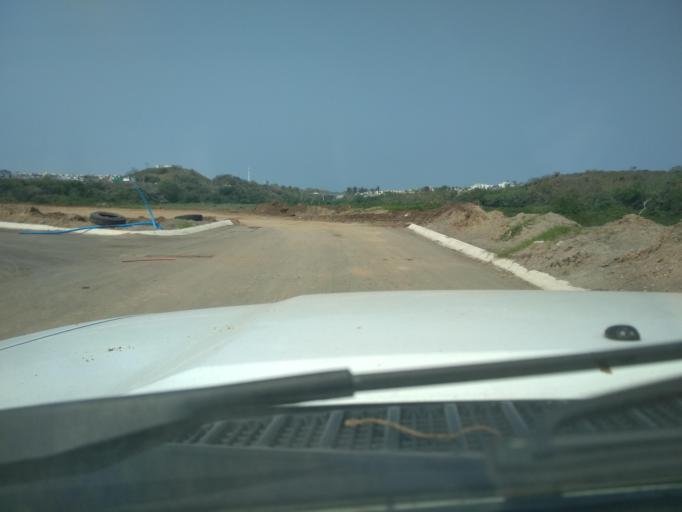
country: MX
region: Veracruz
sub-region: Veracruz
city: Lomas de Rio Medio Cuatro
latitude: 19.1913
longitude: -96.2056
